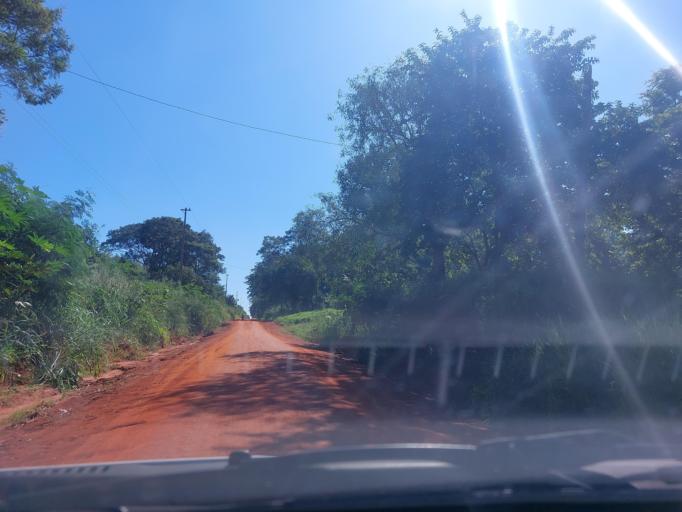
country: PY
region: San Pedro
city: Lima
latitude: -24.1692
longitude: -56.0134
